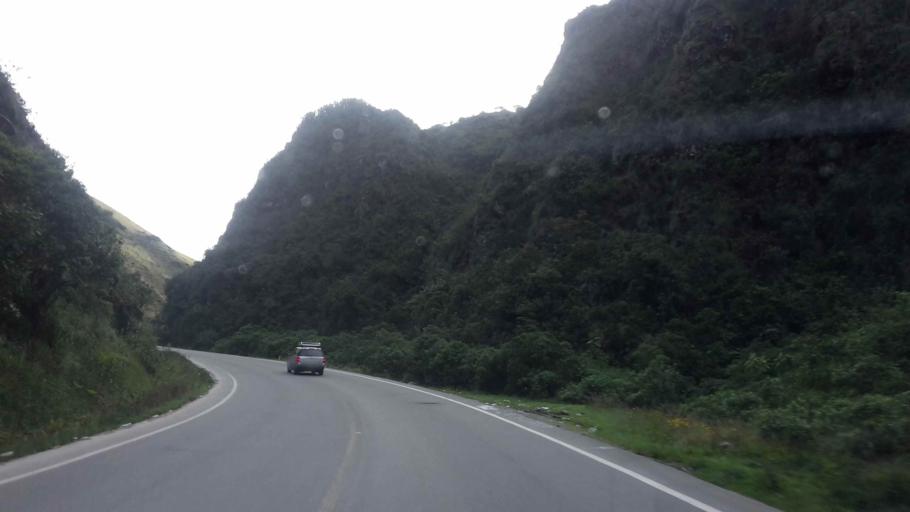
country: BO
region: Cochabamba
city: Colomi
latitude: -17.2127
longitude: -65.8886
